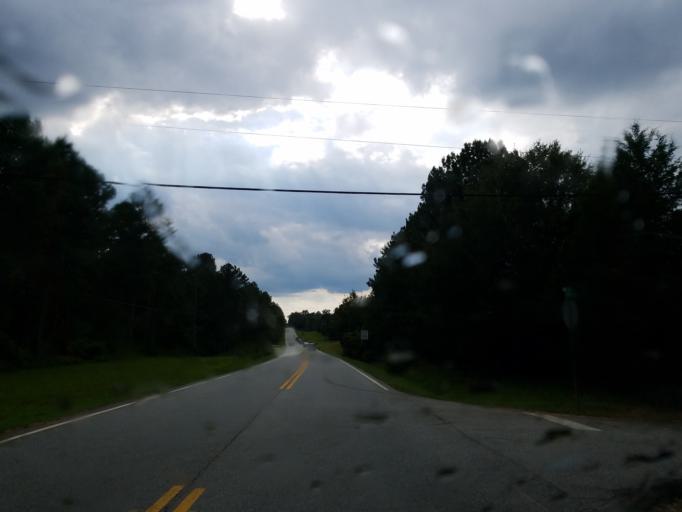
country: US
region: Georgia
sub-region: Floyd County
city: Shannon
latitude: 34.3695
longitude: -85.0852
